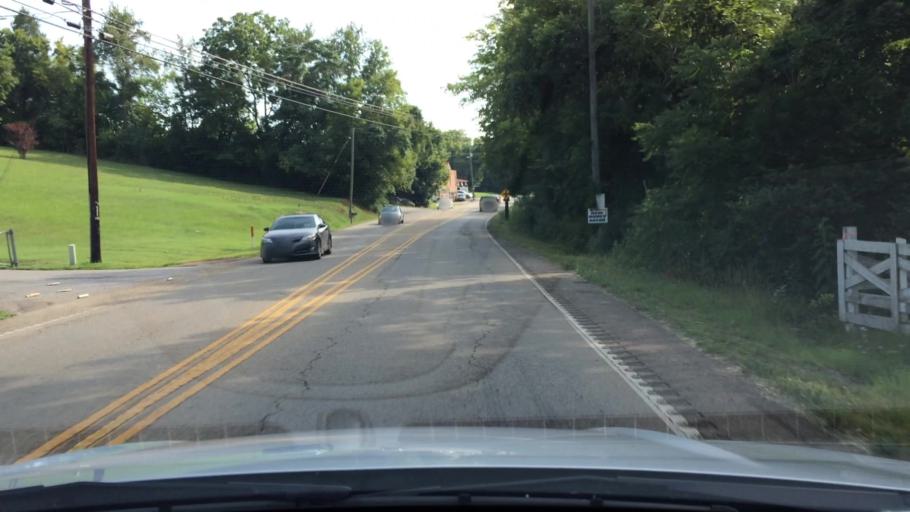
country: US
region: Tennessee
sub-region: Sevier County
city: Seymour
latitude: 35.9197
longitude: -83.6674
